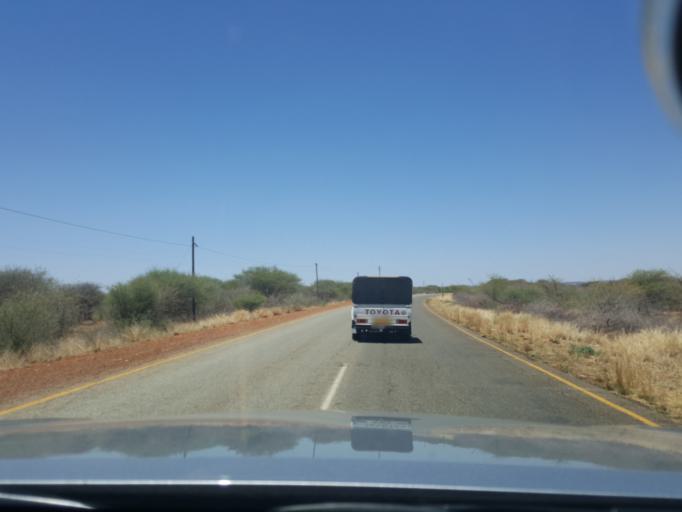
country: BW
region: South East
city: Otse
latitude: -25.1037
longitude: 25.9608
